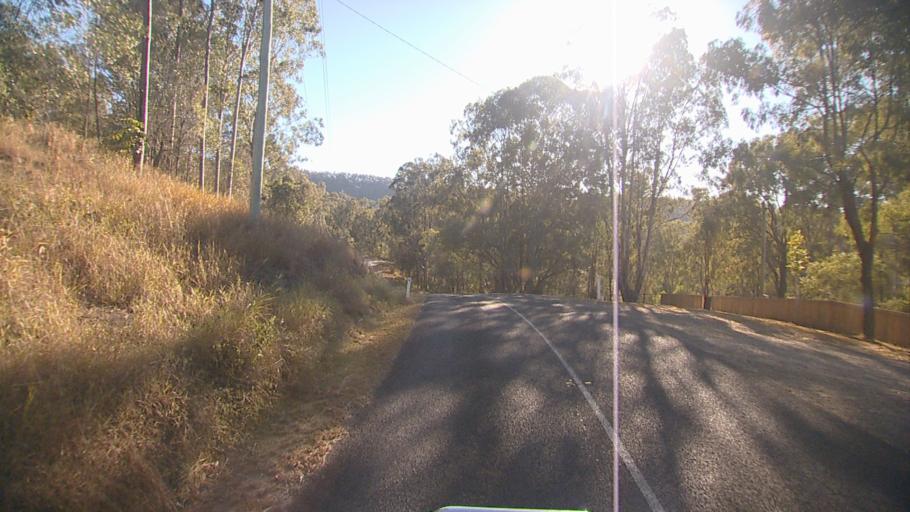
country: AU
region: Queensland
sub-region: Logan
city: Cedar Vale
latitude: -27.8384
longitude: 153.0860
